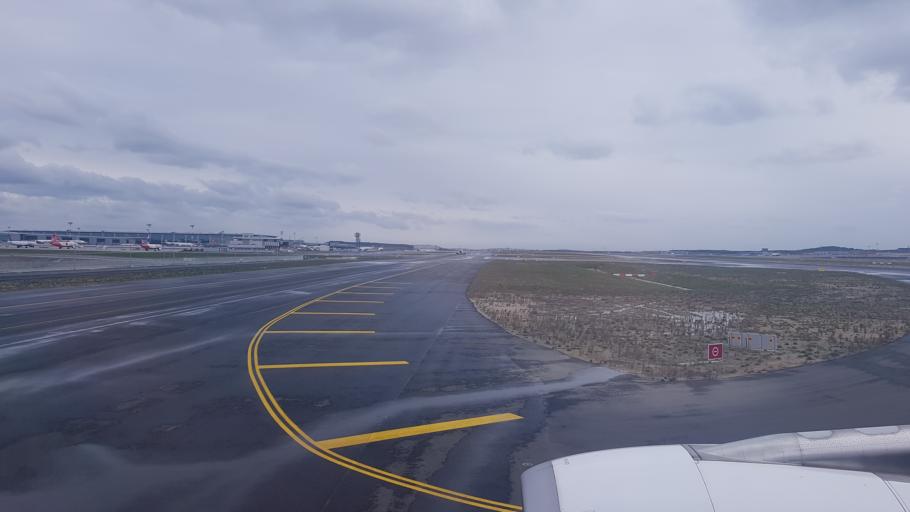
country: TR
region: Istanbul
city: Durusu
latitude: 41.2813
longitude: 28.7290
